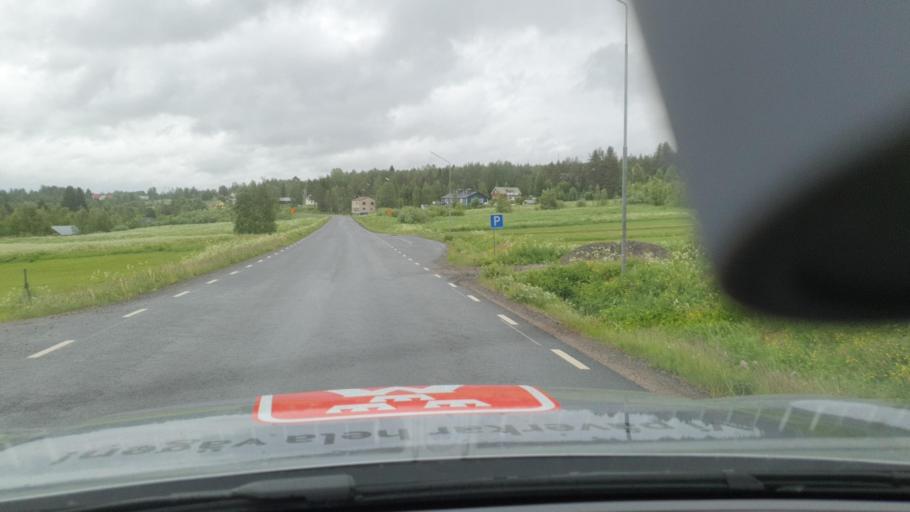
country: FI
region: Lapland
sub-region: Torniolaakso
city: Ylitornio
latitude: 66.1778
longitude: 23.7907
